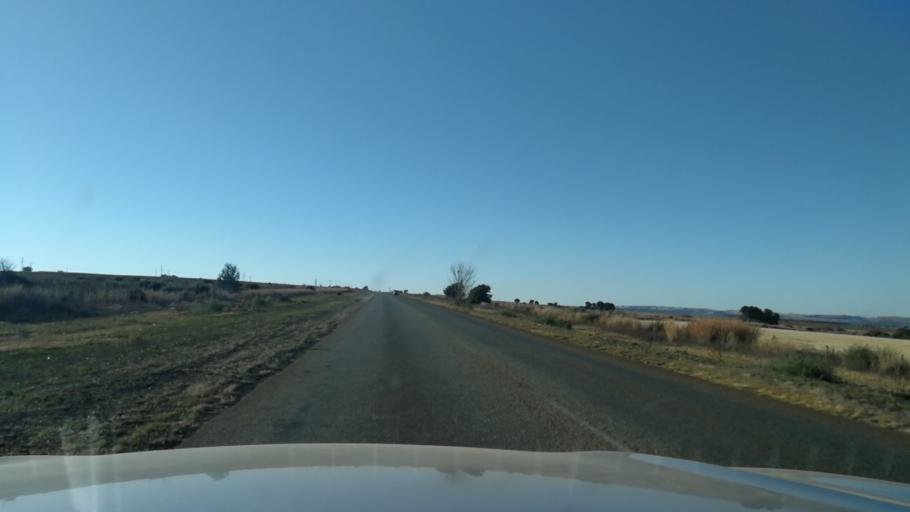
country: ZA
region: North-West
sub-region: Bojanala Platinum District Municipality
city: Rustenburg
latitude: -25.9869
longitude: 27.2777
